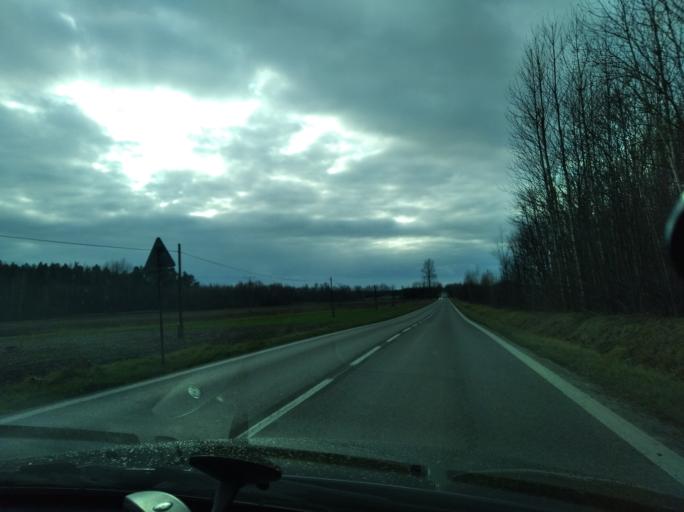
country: PL
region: Subcarpathian Voivodeship
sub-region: Powiat lancucki
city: Rakszawa
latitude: 50.1471
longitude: 22.2706
